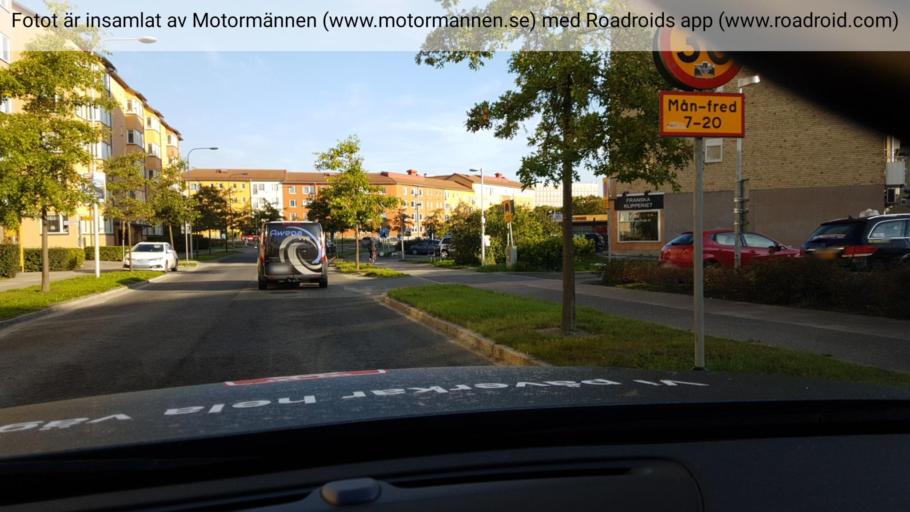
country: SE
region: Stockholm
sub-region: Huddinge Kommun
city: Huddinge
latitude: 59.2397
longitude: 17.9949
